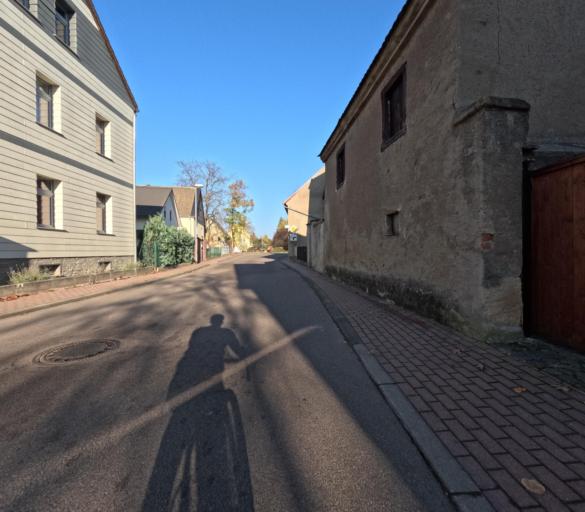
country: DE
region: Saxony
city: Naunhof
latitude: 51.2516
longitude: 12.6372
